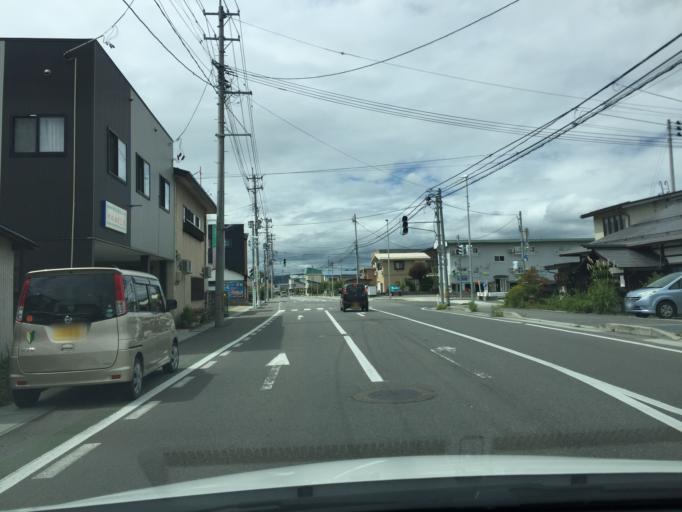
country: JP
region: Yamagata
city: Yonezawa
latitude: 37.9022
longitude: 140.1168
